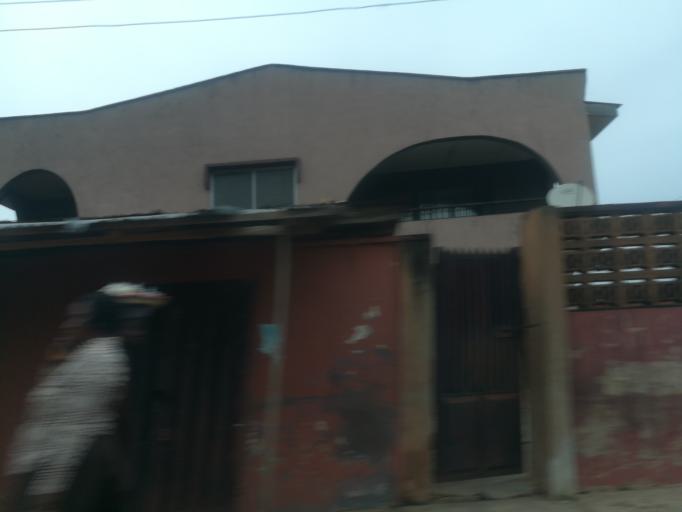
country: NG
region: Oyo
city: Egbeda
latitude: 7.4036
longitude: 3.9792
